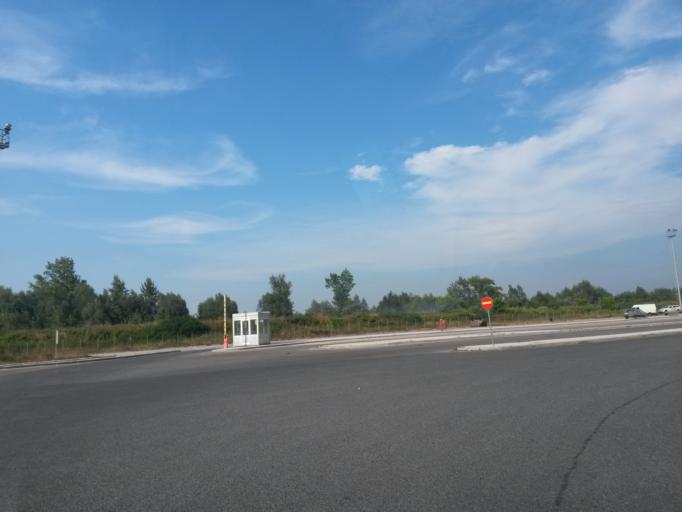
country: HR
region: Brodsko-Posavska
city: Krusevica
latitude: 45.0576
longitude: 18.4887
